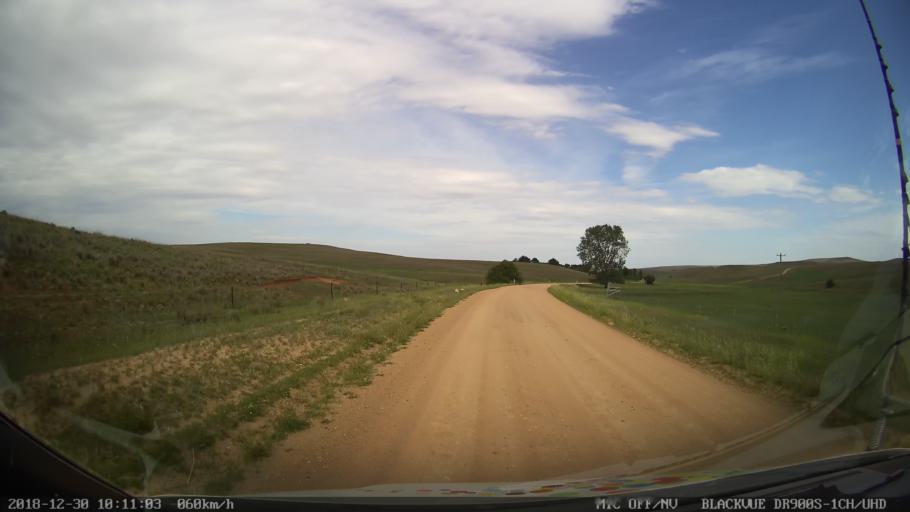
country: AU
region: New South Wales
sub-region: Cooma-Monaro
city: Cooma
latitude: -36.5496
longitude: 149.0884
